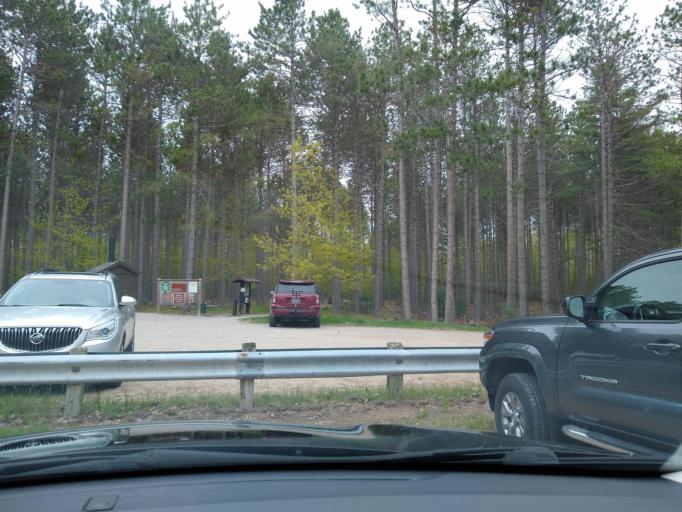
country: US
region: Michigan
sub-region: Delta County
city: Gladstone
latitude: 45.8899
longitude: -87.0468
